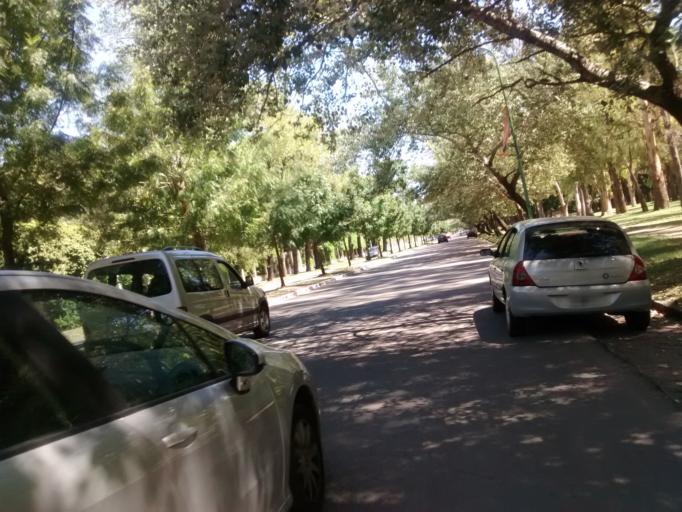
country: AR
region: Buenos Aires
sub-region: Partido de La Plata
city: La Plata
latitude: -34.9044
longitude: -57.9360
